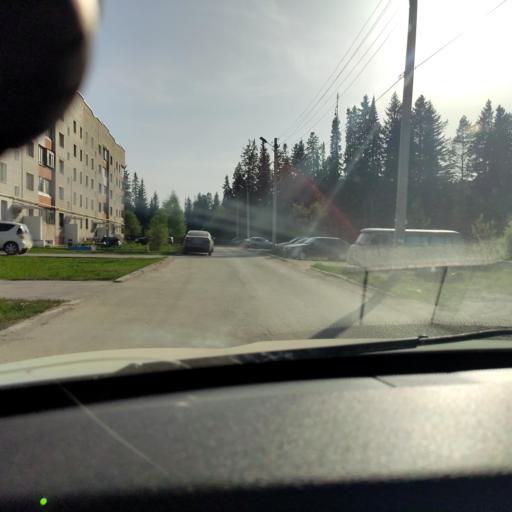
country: RU
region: Perm
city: Polazna
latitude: 58.2974
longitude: 56.3895
